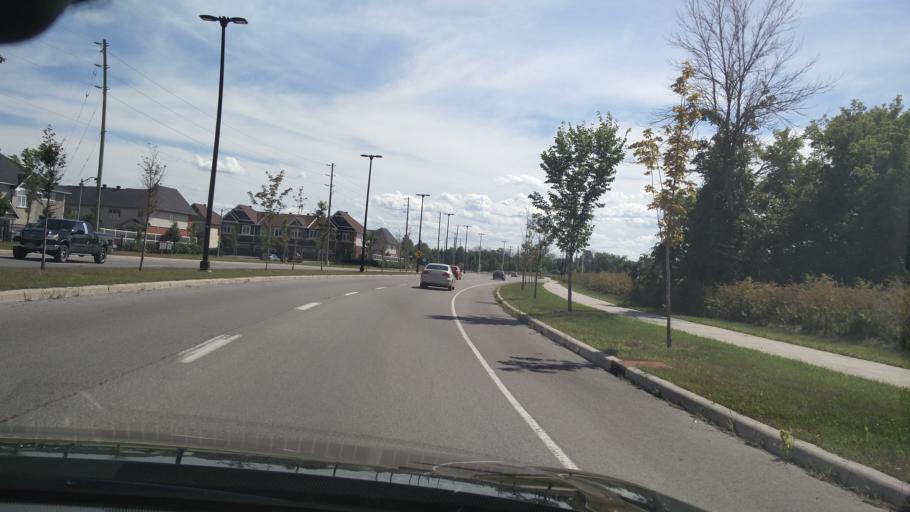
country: CA
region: Ontario
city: Bells Corners
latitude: 45.2672
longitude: -75.7344
